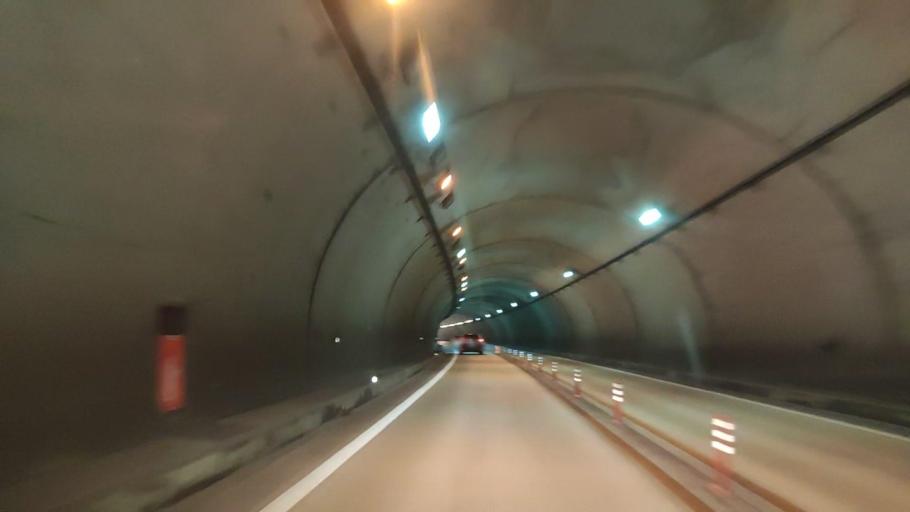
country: JP
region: Hiroshima
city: Innoshima
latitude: 34.2936
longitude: 133.1436
